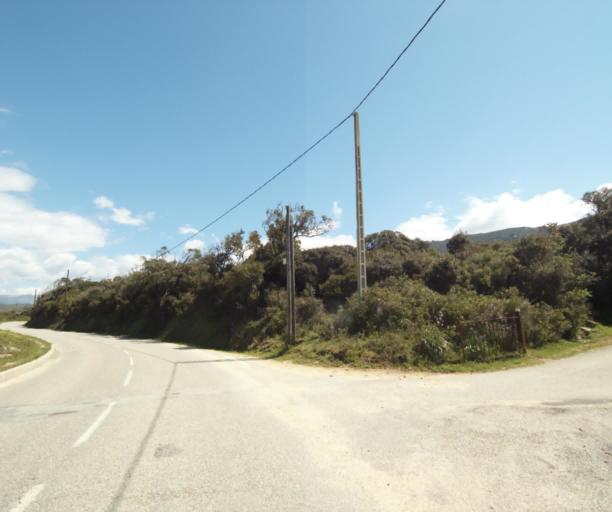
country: FR
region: Corsica
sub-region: Departement de la Corse-du-Sud
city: Propriano
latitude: 41.6453
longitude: 8.8719
